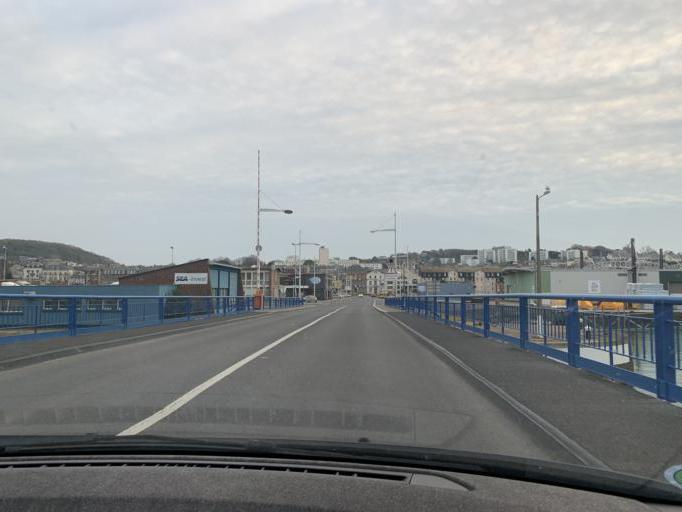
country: FR
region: Haute-Normandie
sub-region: Departement de la Seine-Maritime
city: Fecamp
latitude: 49.7618
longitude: 0.3742
